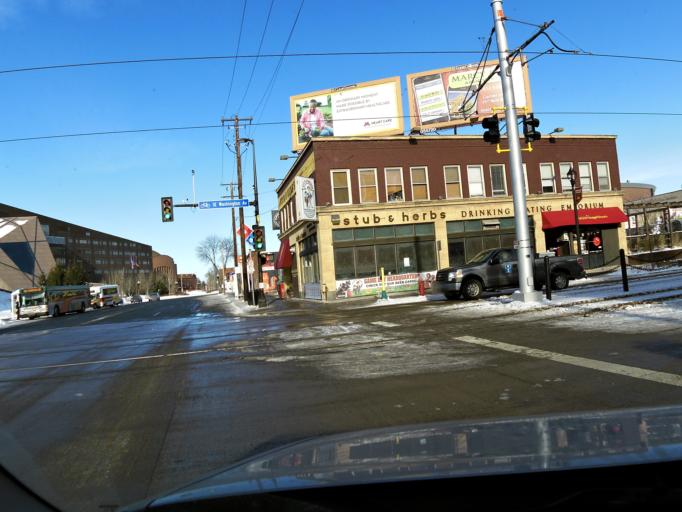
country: US
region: Minnesota
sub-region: Ramsey County
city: Lauderdale
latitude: 44.9736
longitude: -93.2271
